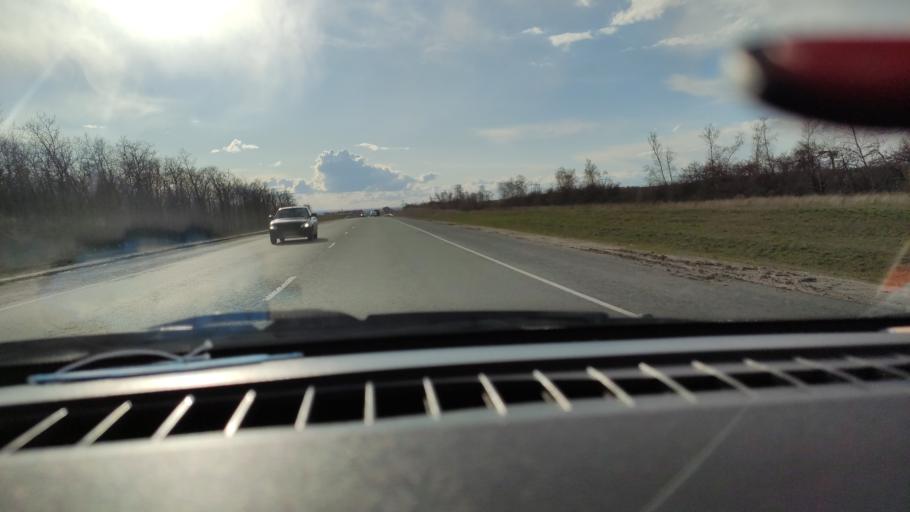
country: RU
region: Saratov
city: Yelshanka
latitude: 51.8219
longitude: 46.3323
